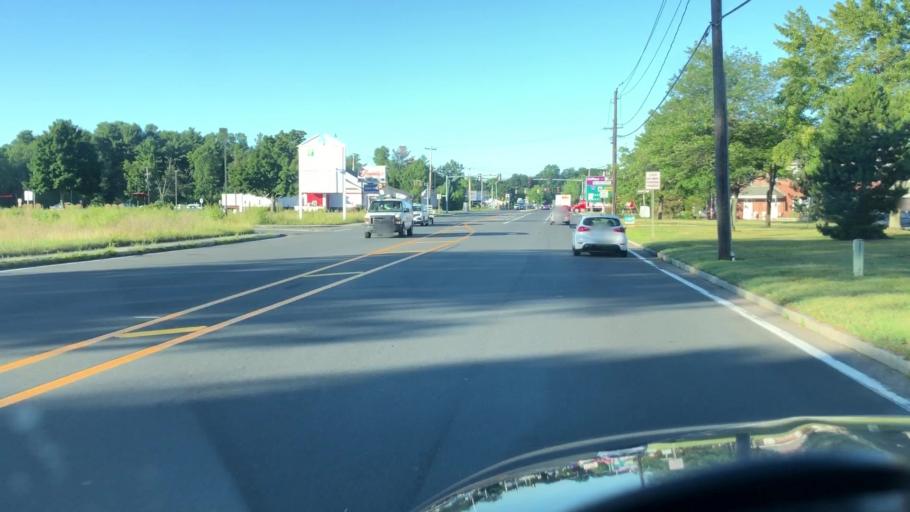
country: US
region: Massachusetts
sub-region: Hampden County
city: Westfield
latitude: 42.1431
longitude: -72.7323
